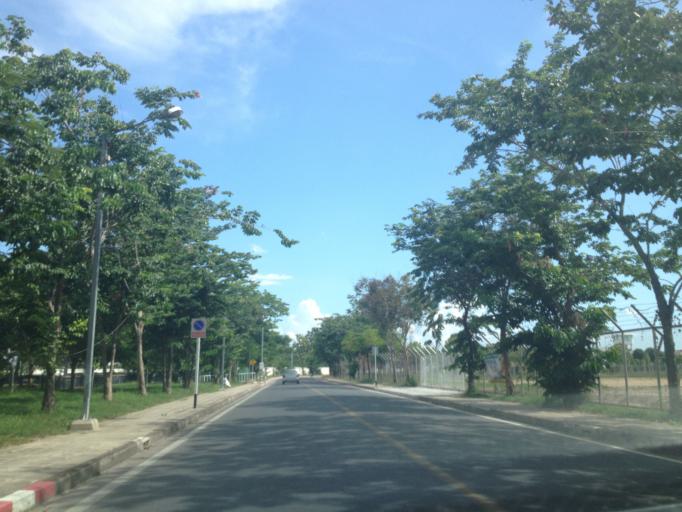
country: TH
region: Chiang Mai
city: Chiang Mai
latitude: 18.7649
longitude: 98.9690
